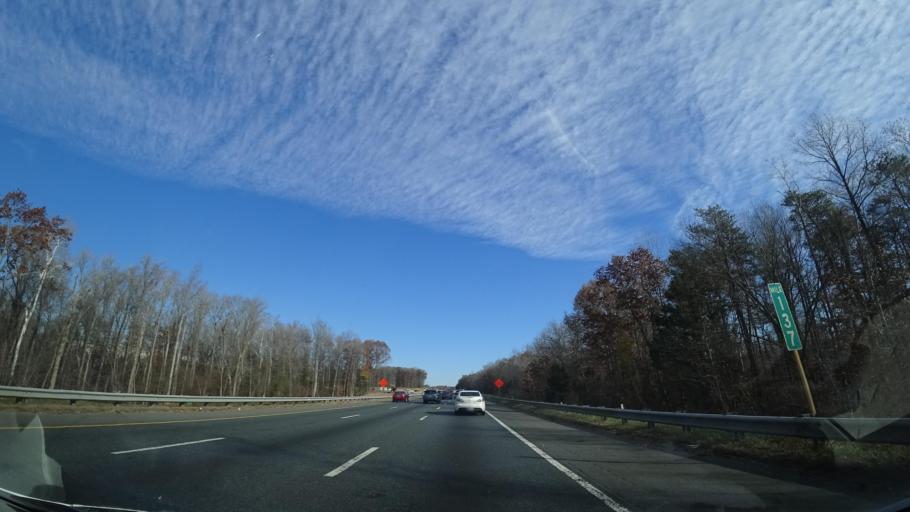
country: US
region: Virginia
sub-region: Stafford County
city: Falmouth
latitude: 38.3793
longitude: -77.4545
